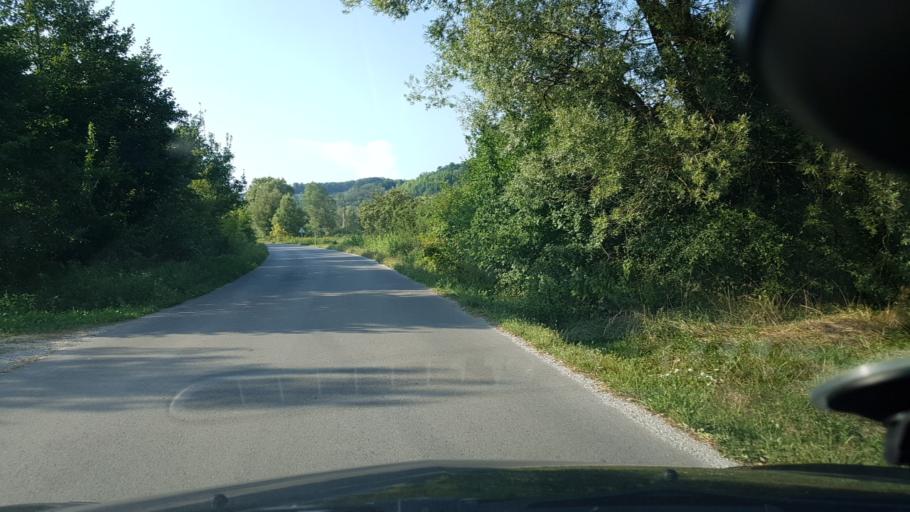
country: HR
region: Krapinsko-Zagorska
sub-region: Grad Krapina
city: Krapina
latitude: 46.1161
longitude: 15.8622
